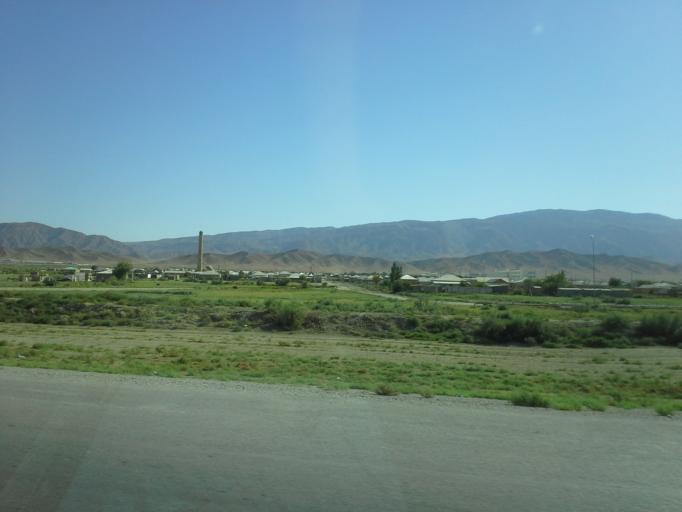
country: TM
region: Ahal
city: Baharly
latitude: 38.3790
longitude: 57.5040
